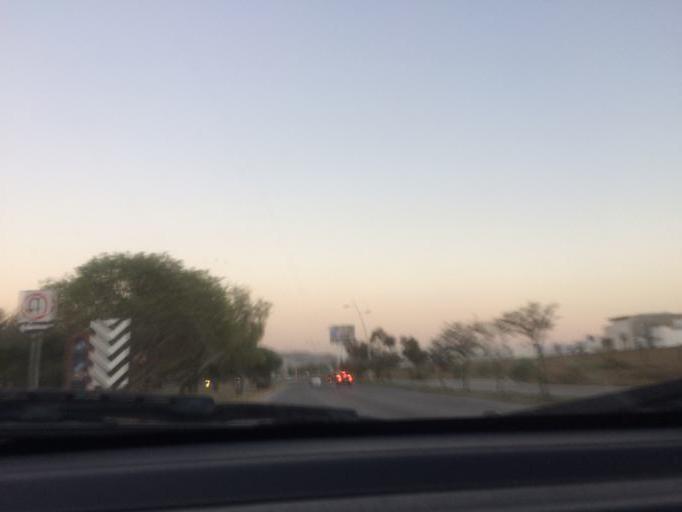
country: MX
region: Guanajuato
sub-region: Leon
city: Medina
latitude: 21.1315
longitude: -101.6085
